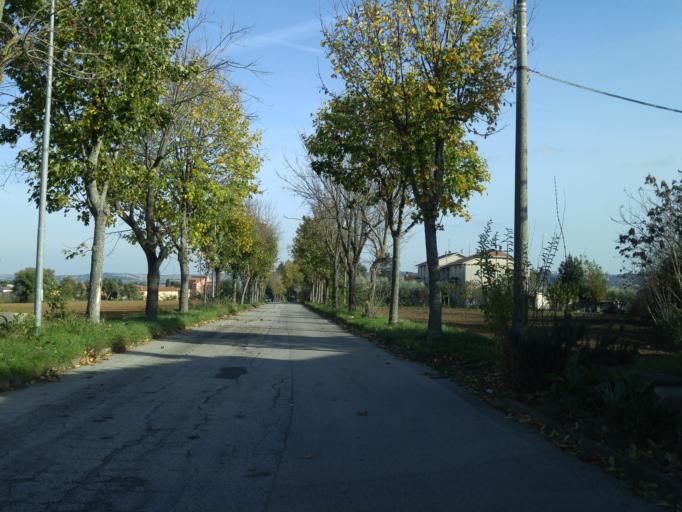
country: IT
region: The Marches
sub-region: Provincia di Pesaro e Urbino
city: Saltara
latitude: 43.7511
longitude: 12.9041
